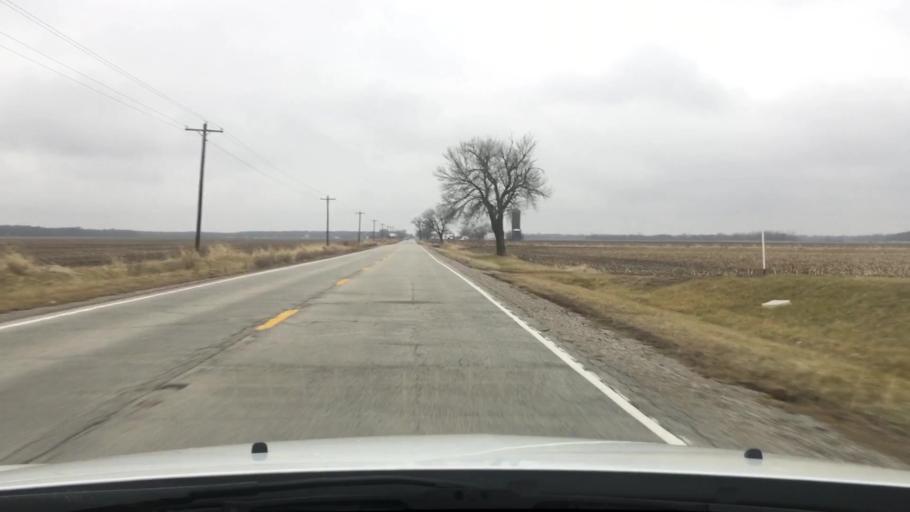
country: US
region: Illinois
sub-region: Iroquois County
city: Watseka
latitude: 40.8886
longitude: -87.7952
